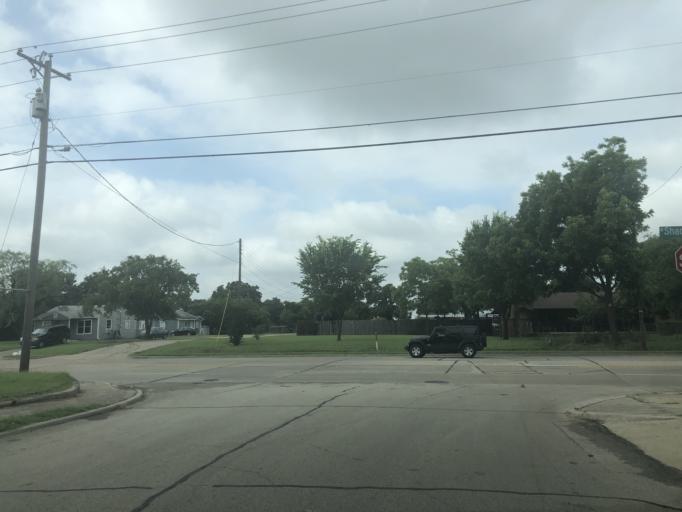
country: US
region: Texas
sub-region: Dallas County
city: Irving
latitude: 32.8032
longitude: -96.9884
